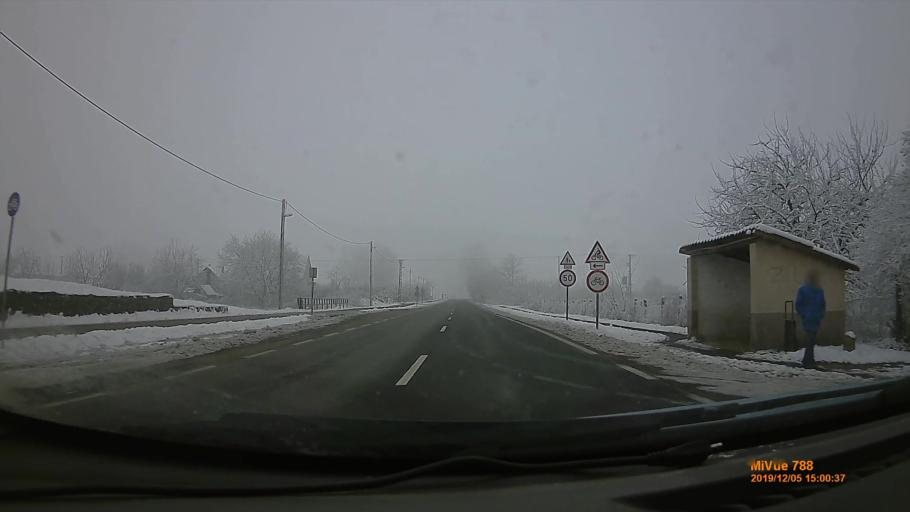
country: HU
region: Szabolcs-Szatmar-Bereg
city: Tiszanagyfalu
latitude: 48.0650
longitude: 21.5379
